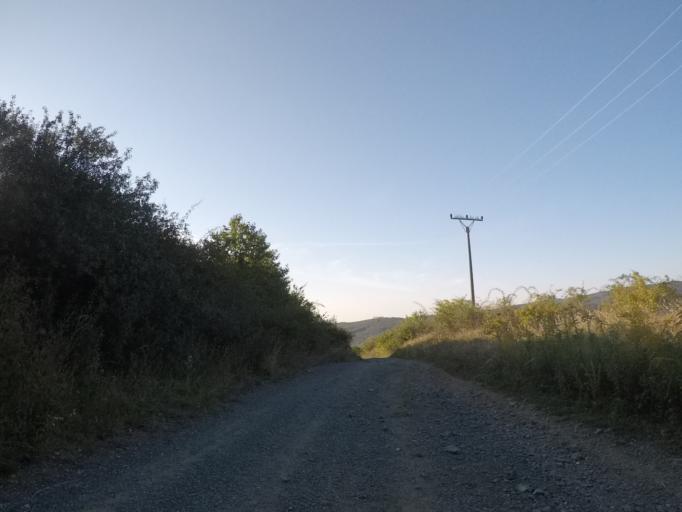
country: SK
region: Kosicky
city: Kosice
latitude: 48.7362
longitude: 21.1376
